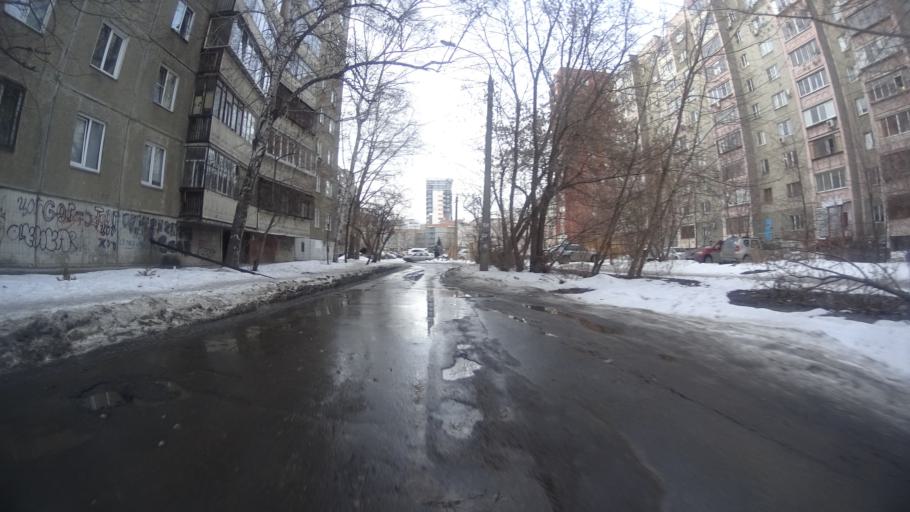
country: RU
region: Chelyabinsk
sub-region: Gorod Chelyabinsk
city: Chelyabinsk
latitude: 55.1768
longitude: 61.3472
